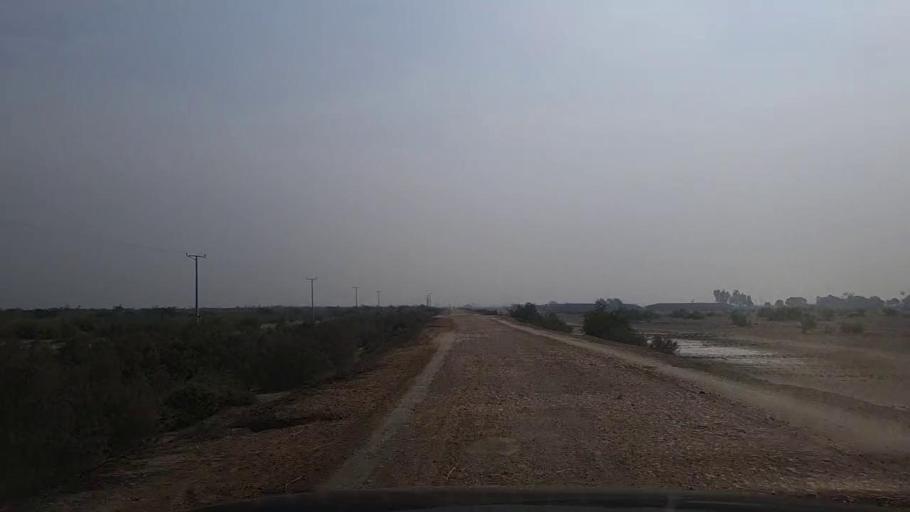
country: PK
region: Sindh
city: Mirpur Sakro
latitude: 24.3927
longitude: 67.7513
